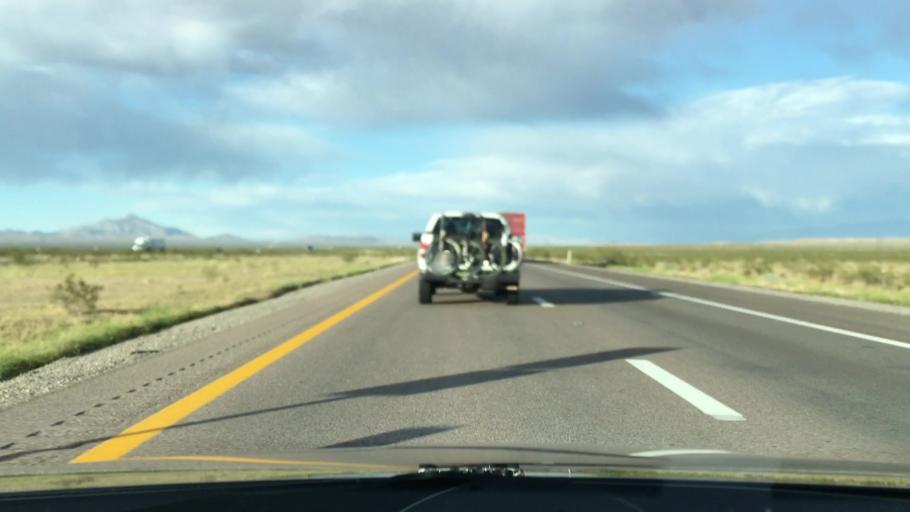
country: US
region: Nevada
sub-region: Clark County
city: Moapa Town
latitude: 36.7085
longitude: -114.4787
